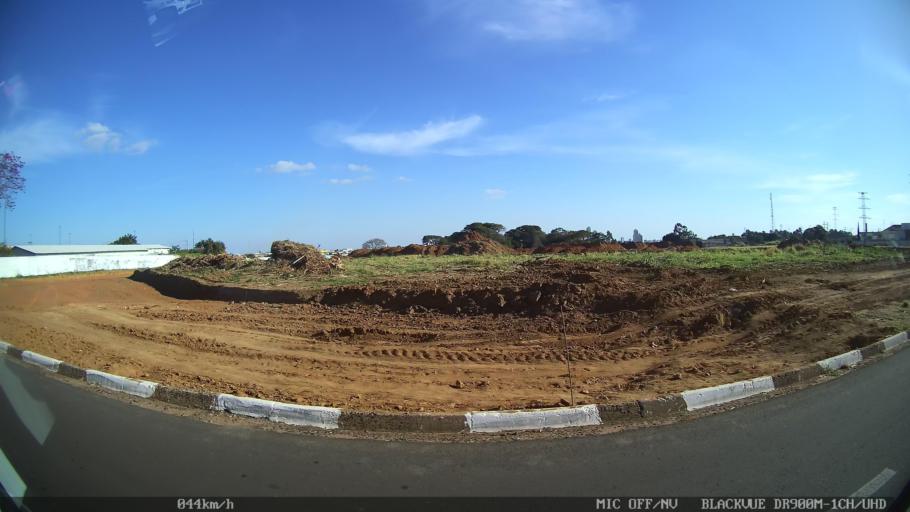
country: BR
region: Sao Paulo
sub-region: Franca
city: Franca
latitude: -20.5146
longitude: -47.3741
